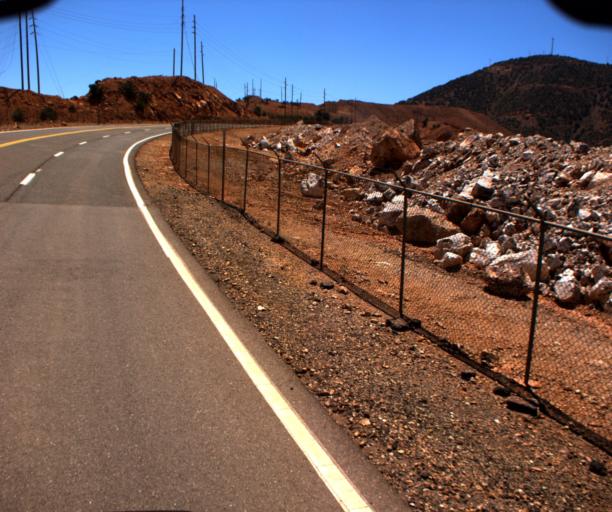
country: US
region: Arizona
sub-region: Greenlee County
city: Morenci
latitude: 33.1073
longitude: -109.3766
